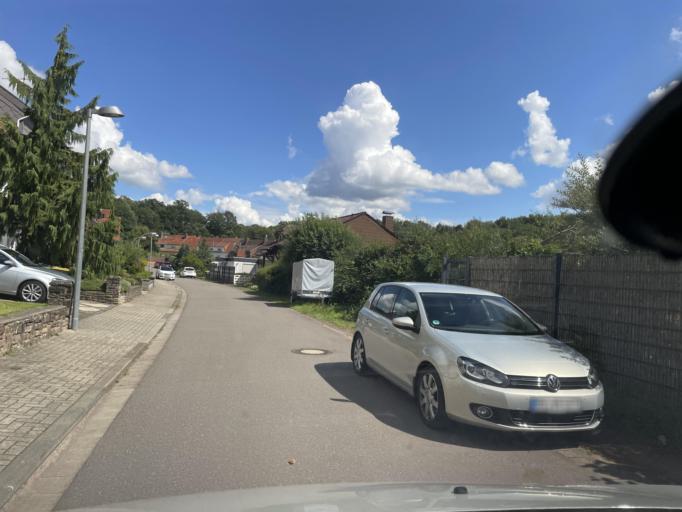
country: DE
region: Saarland
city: Sulzbach
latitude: 49.2720
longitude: 7.0547
